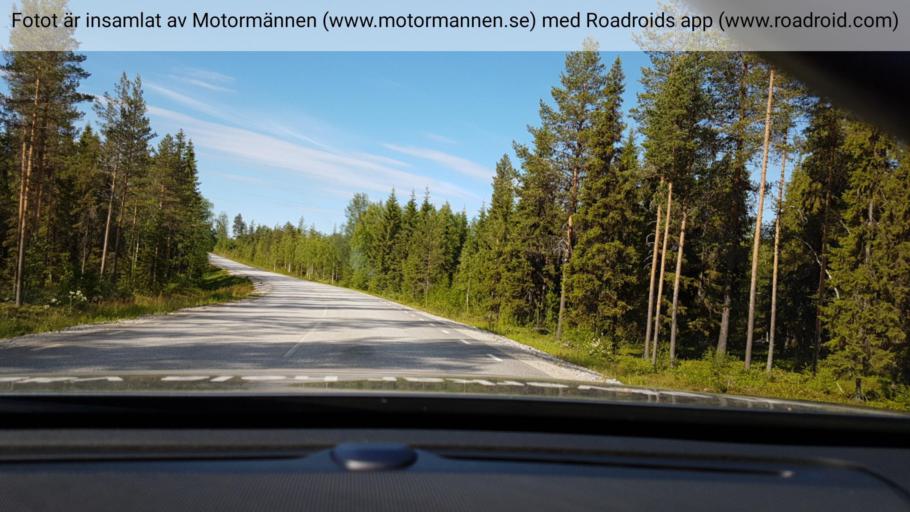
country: SE
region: Vaesterbotten
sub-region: Bjurholms Kommun
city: Bjurholm
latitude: 64.1547
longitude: 19.3555
